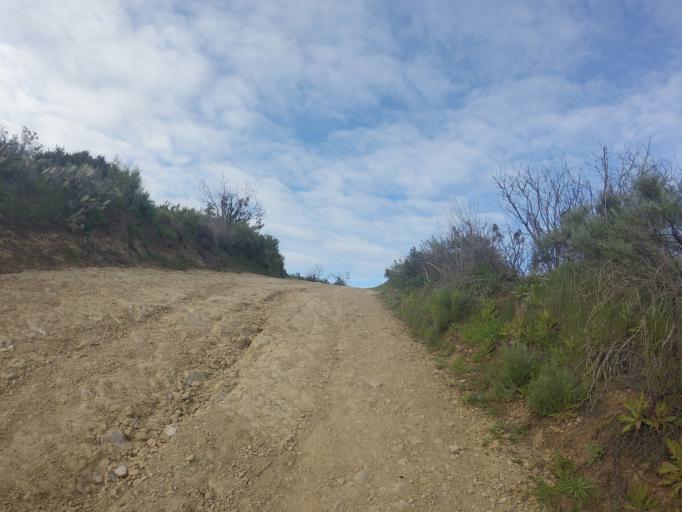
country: US
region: California
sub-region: Orange County
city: Aliso Viejo
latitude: 33.5844
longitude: -117.7654
